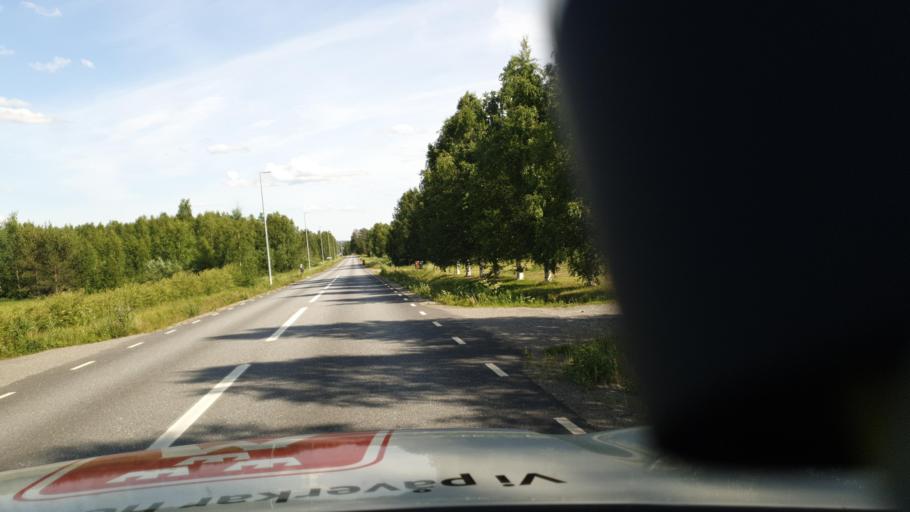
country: SE
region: Vaesterbotten
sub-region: Skelleftea Kommun
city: Forsbacka
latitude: 64.6929
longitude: 20.4970
